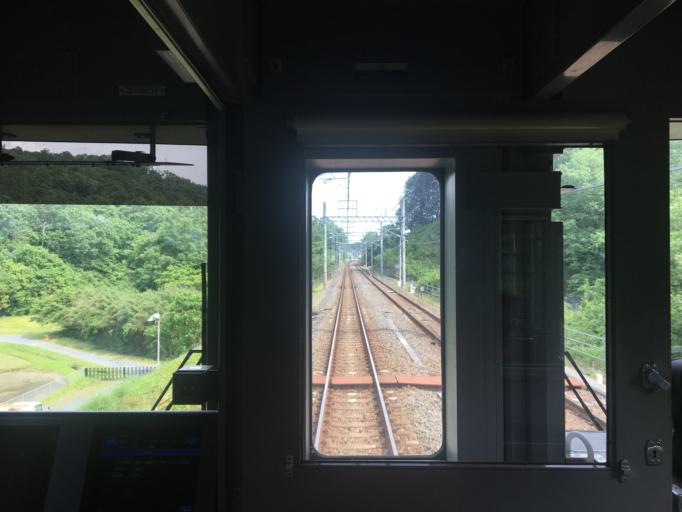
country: JP
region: Saitama
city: Ogawa
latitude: 36.0554
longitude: 139.3010
